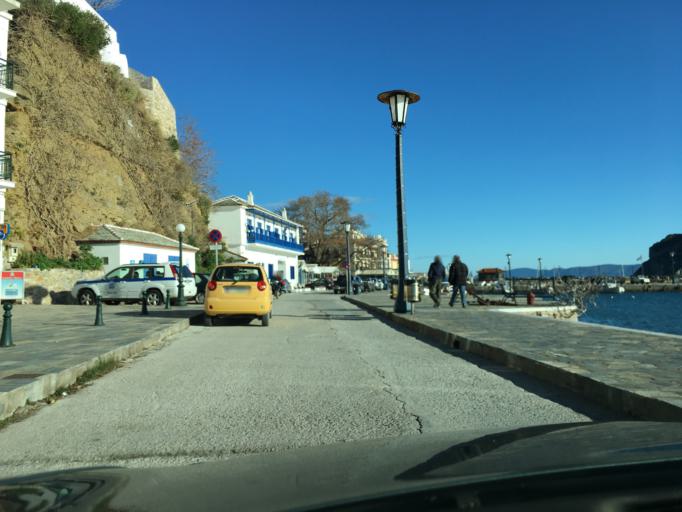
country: GR
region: Thessaly
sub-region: Nomos Magnisias
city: Skopelos
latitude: 39.1229
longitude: 23.7284
